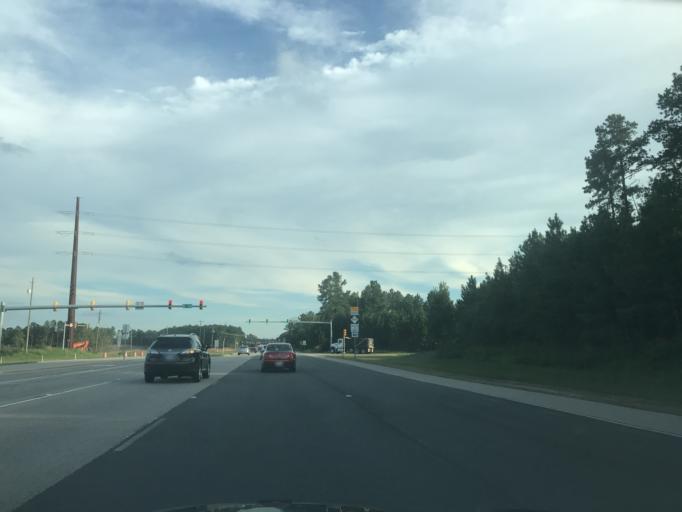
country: US
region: North Carolina
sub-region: Wake County
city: Green Level
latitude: 35.8398
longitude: -78.8860
